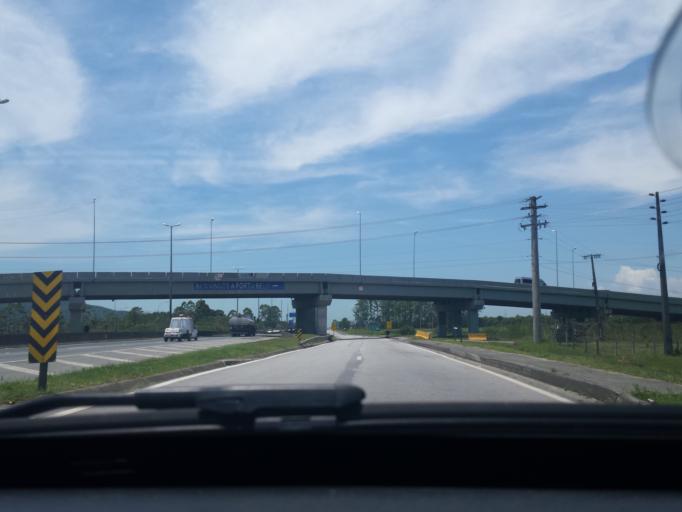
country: BR
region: Santa Catarina
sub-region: Porto Belo
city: Porto Belo
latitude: -27.1621
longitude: -48.6113
